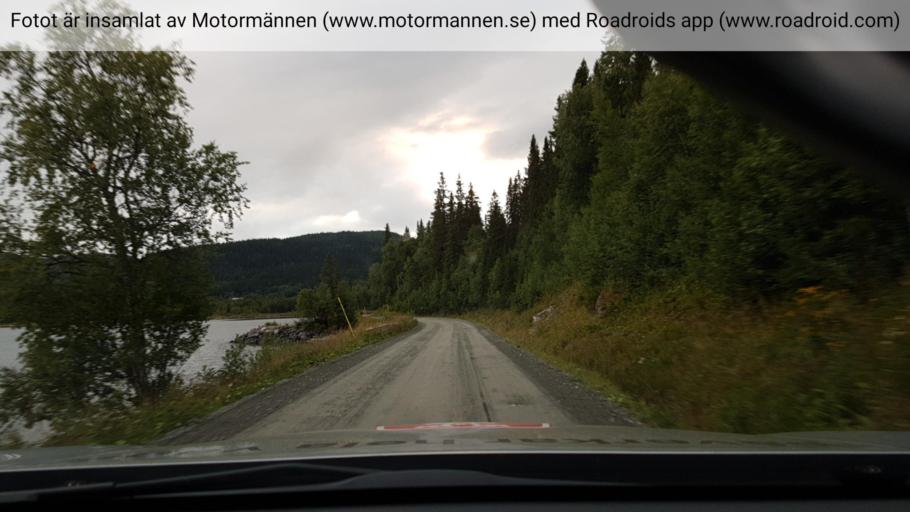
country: NO
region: Nordland
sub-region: Hattfjelldal
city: Hattfjelldal
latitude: 65.6561
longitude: 15.1553
